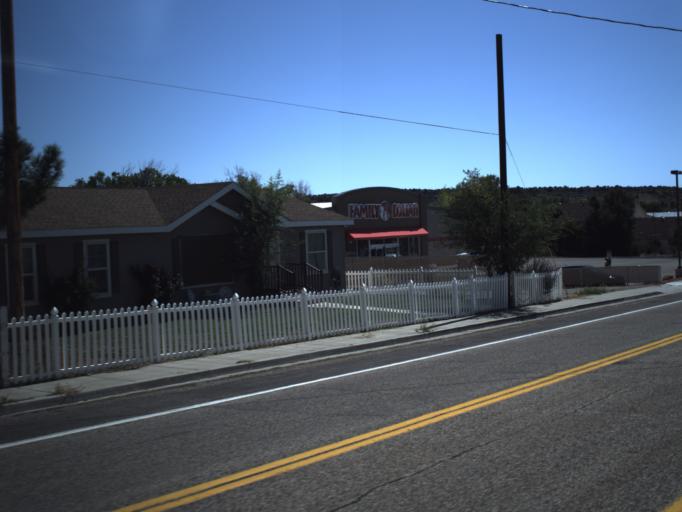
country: US
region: Utah
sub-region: Washington County
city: Ivins
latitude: 37.3395
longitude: -113.6933
